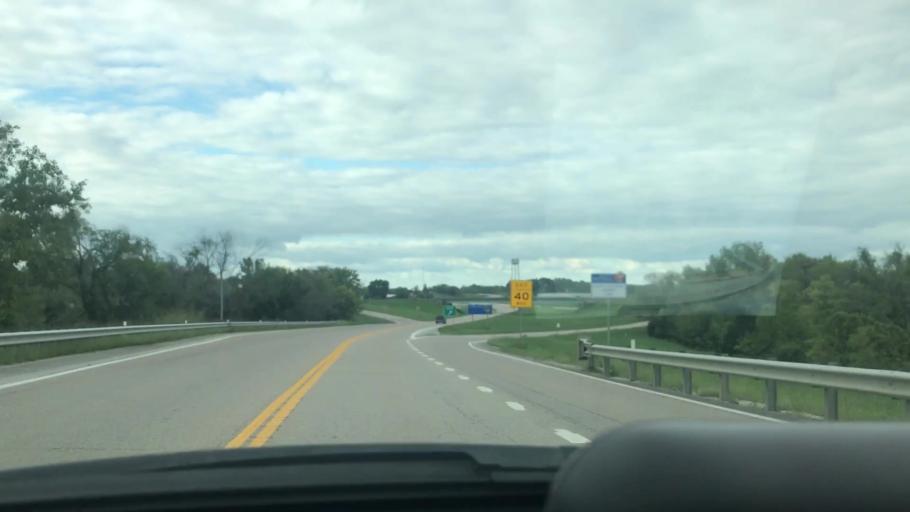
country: US
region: Missouri
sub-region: Benton County
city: Warsaw
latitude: 38.2388
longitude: -93.3603
